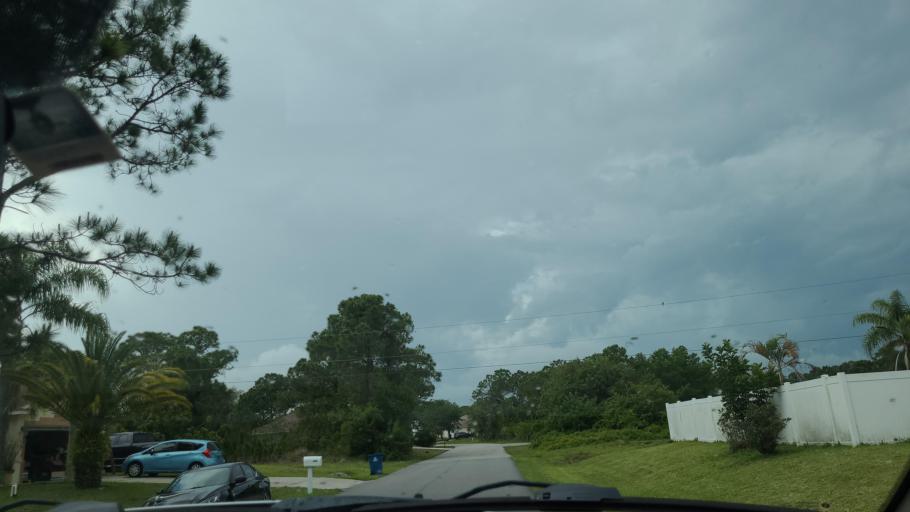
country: US
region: Florida
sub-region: Brevard County
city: Grant-Valkaria
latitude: 27.9466
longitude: -80.6335
